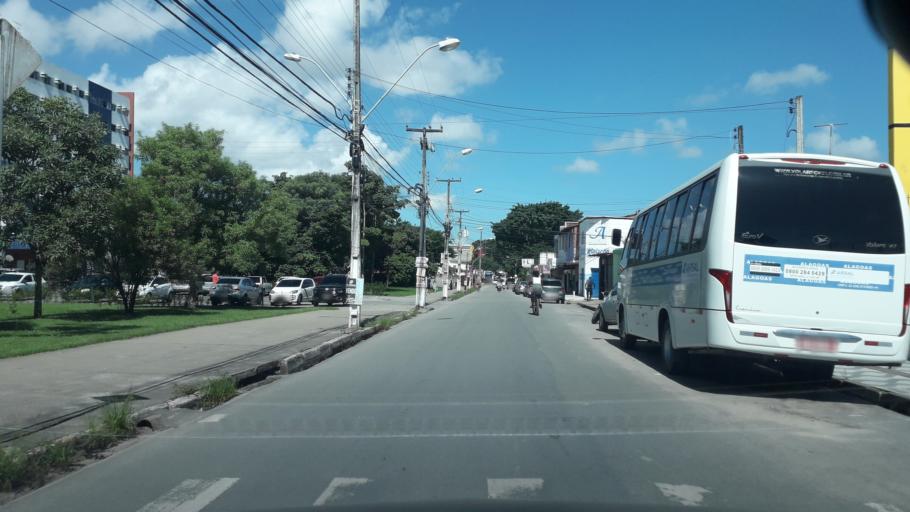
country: BR
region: Alagoas
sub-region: Satuba
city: Satuba
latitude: -9.5801
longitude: -35.7703
